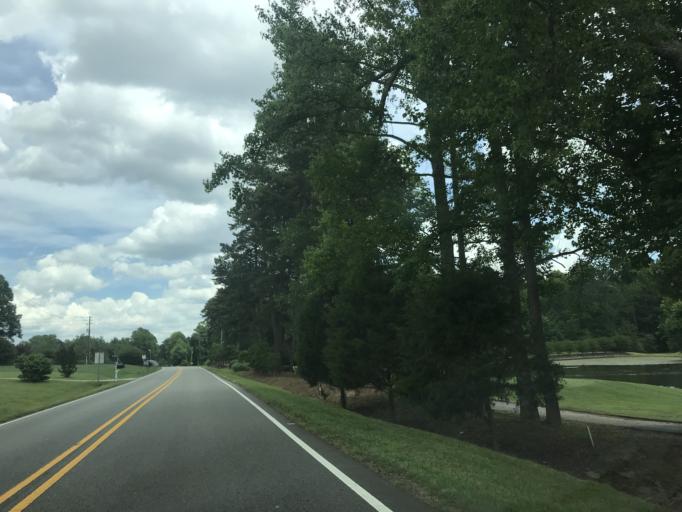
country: US
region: North Carolina
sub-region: Wake County
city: West Raleigh
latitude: 35.9133
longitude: -78.6865
